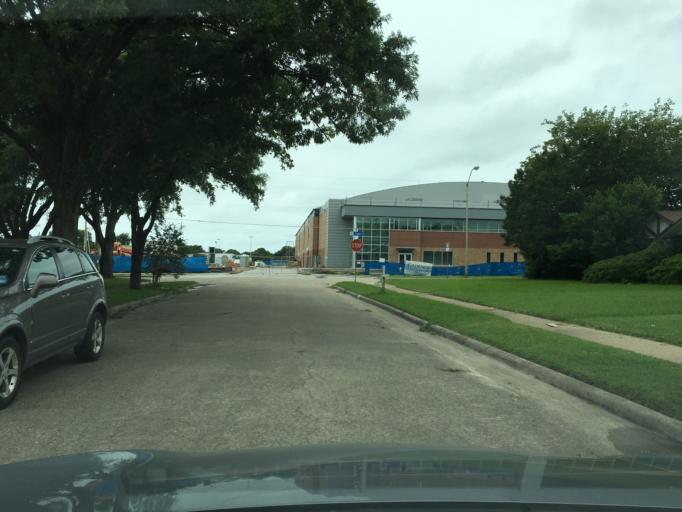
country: US
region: Texas
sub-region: Dallas County
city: Richardson
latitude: 32.9344
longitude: -96.6904
